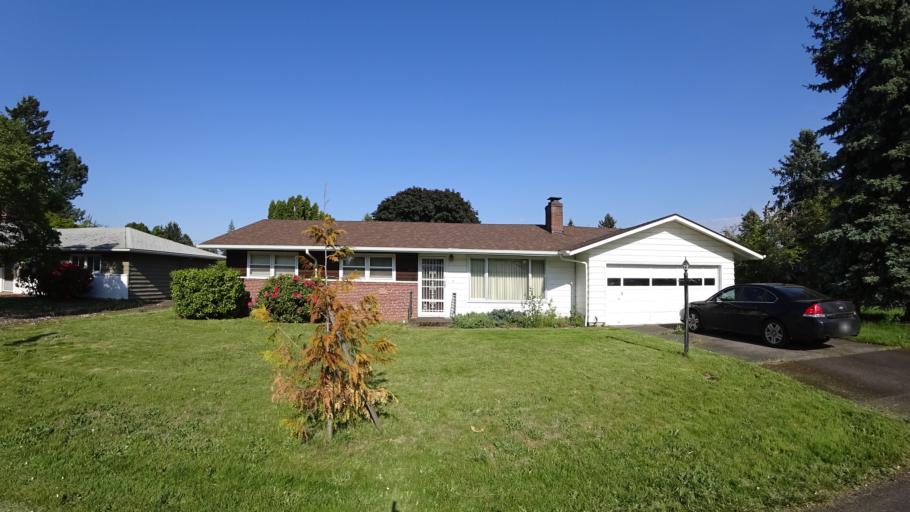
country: US
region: Oregon
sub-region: Clackamas County
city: Happy Valley
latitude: 45.5073
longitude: -122.5004
